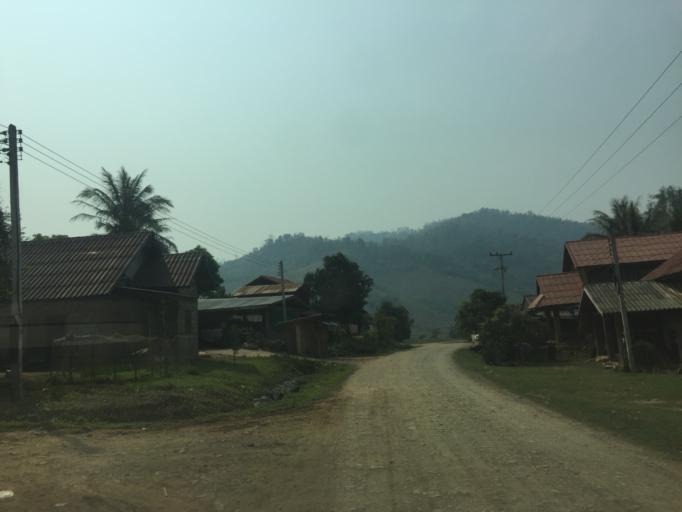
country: TH
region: Phayao
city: Phu Sang
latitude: 19.6115
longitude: 100.5392
